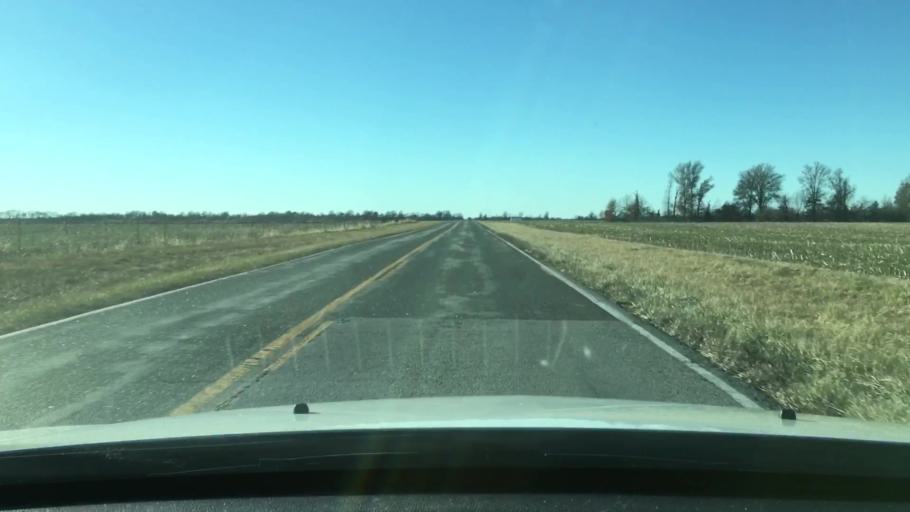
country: US
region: Missouri
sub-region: Audrain County
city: Vandalia
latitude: 39.2813
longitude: -91.6702
